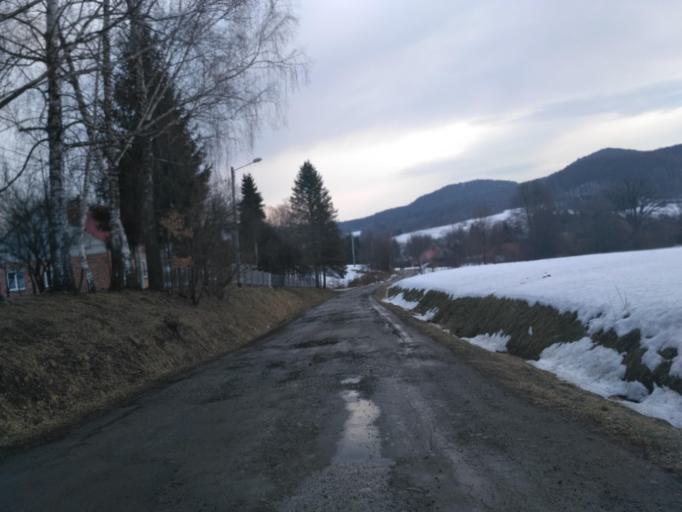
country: PL
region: Subcarpathian Voivodeship
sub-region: Powiat brzozowski
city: Dydnia
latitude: 49.6347
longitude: 22.1668
